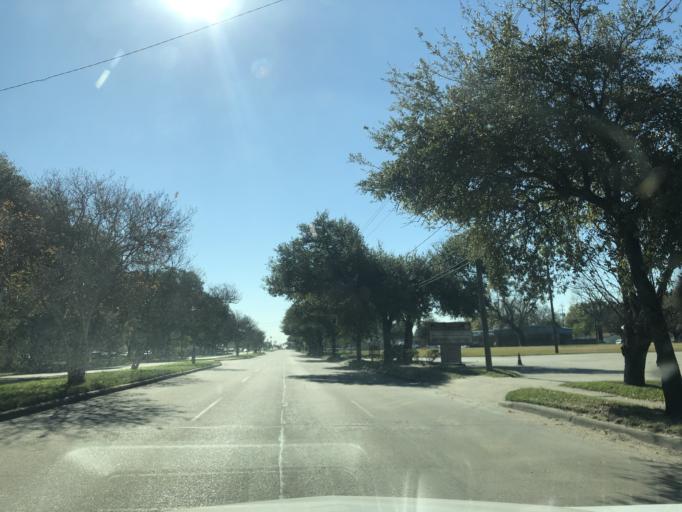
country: US
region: Texas
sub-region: Harris County
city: Houston
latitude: 29.8222
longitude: -95.3021
